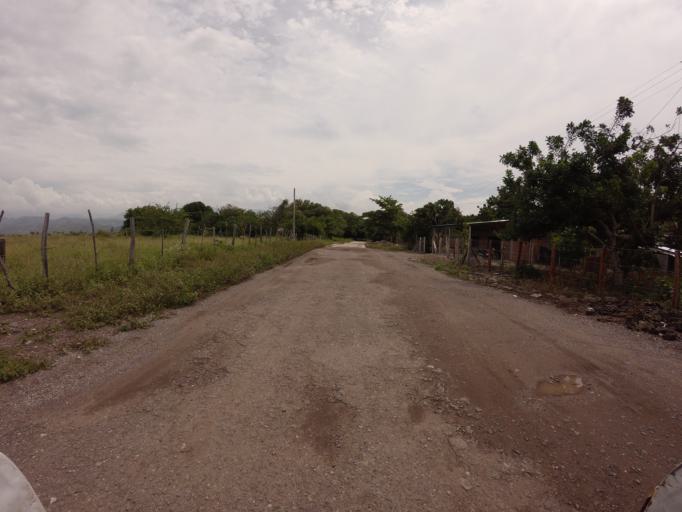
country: CO
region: Tolima
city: Natagaima
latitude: 3.4627
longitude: -75.1402
